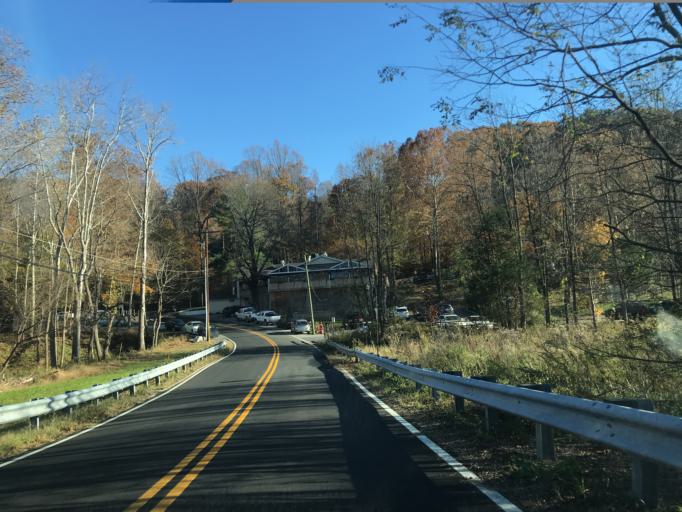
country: US
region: Maryland
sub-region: Baltimore County
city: Carney
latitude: 39.4221
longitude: -76.5381
